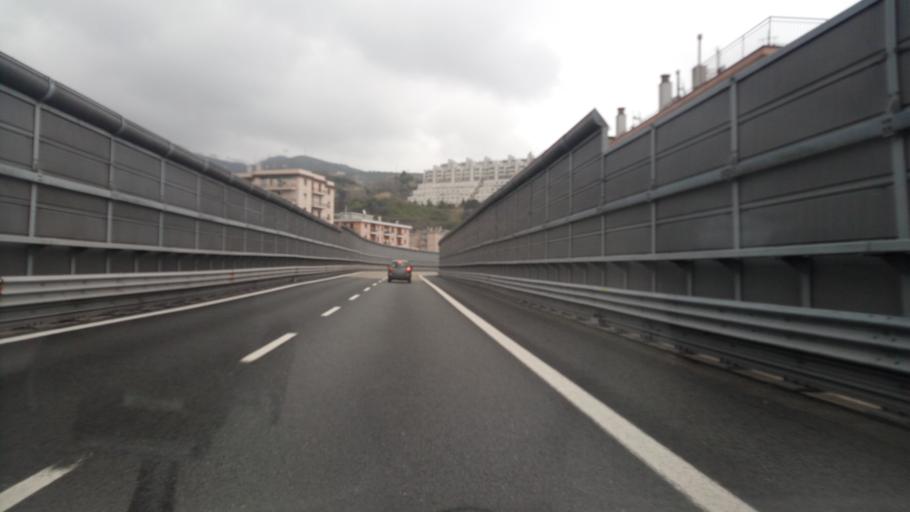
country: IT
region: Liguria
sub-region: Provincia di Genova
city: Mele
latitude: 44.4295
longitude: 8.7873
